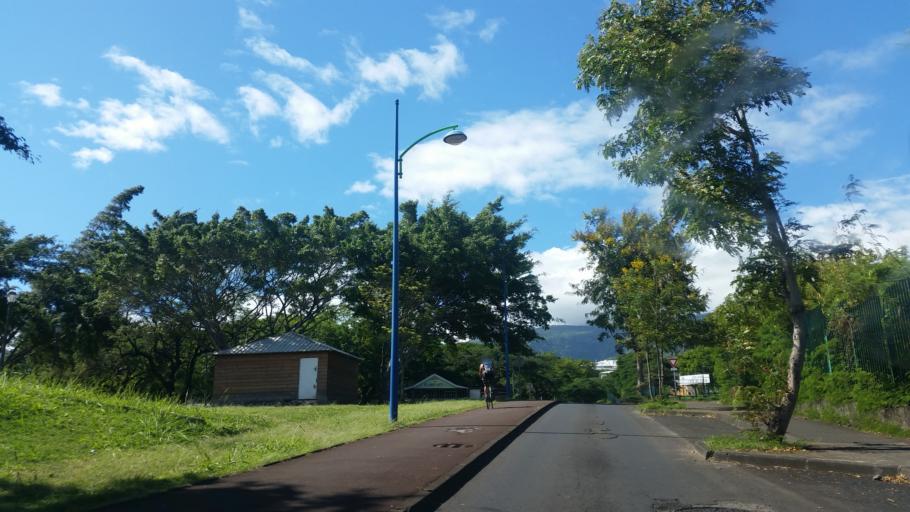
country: RE
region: Reunion
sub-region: Reunion
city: Saint-Denis
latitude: -20.8979
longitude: 55.4861
